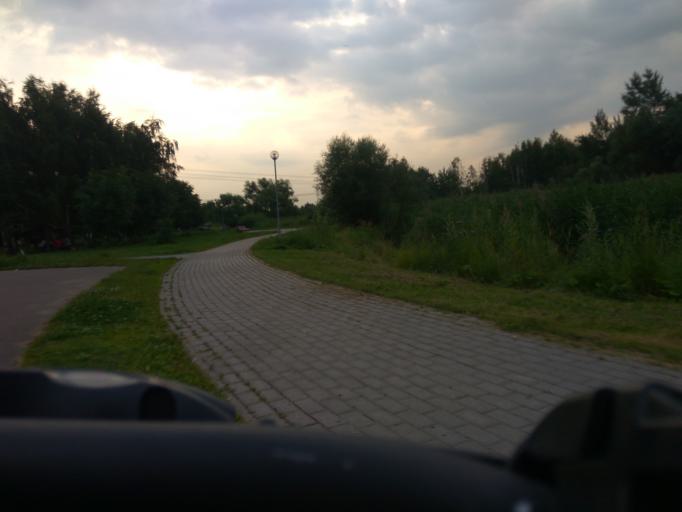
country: RU
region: Moscow
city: Brateyevo
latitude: 55.6309
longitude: 37.7710
